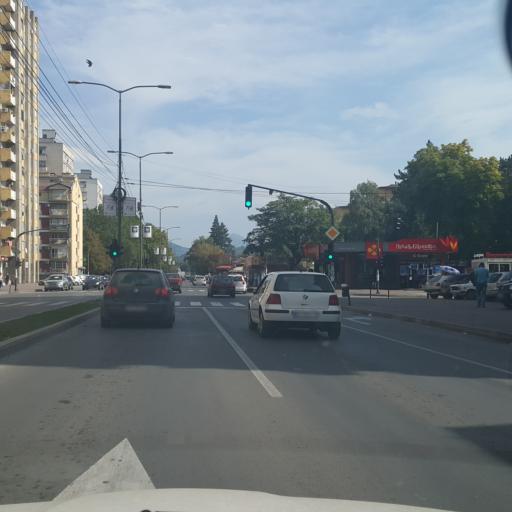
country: RS
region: Central Serbia
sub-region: Nisavski Okrug
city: Nis
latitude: 43.3180
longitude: 21.9107
